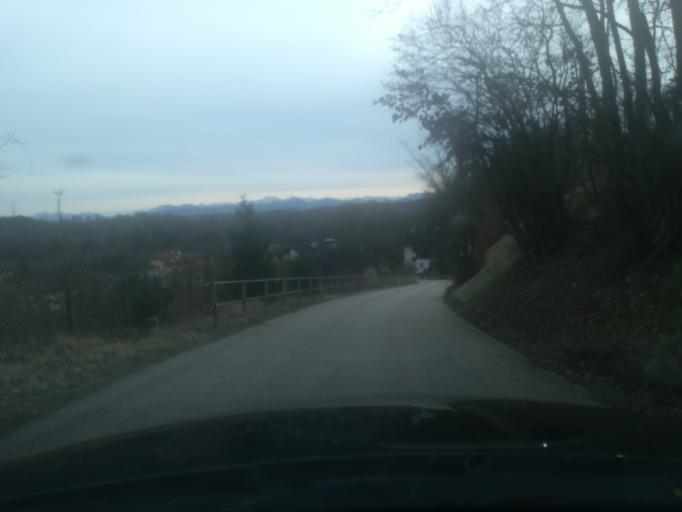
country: AT
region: Upper Austria
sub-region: Wels-Land
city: Gunskirchen
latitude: 48.1103
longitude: 13.9394
